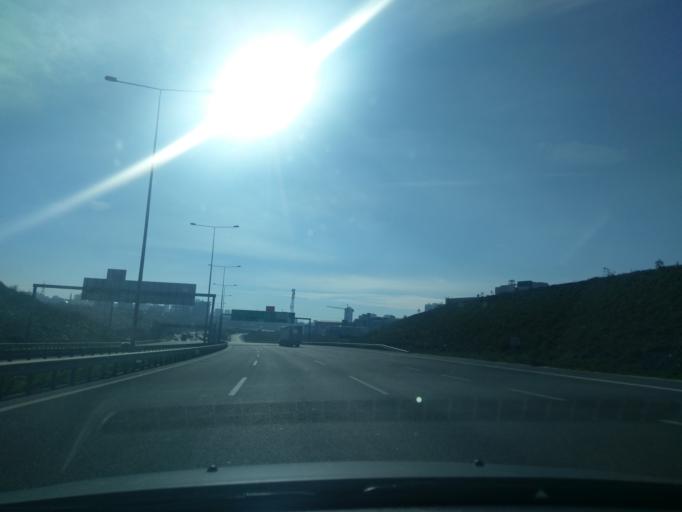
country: TR
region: Istanbul
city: Basaksehir
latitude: 41.0813
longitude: 28.8129
